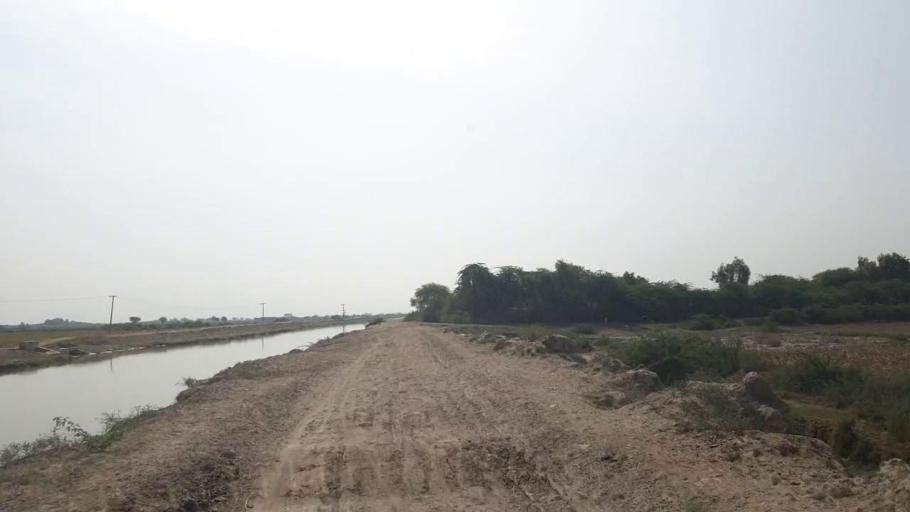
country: PK
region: Sindh
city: Badin
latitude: 24.5522
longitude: 68.8498
